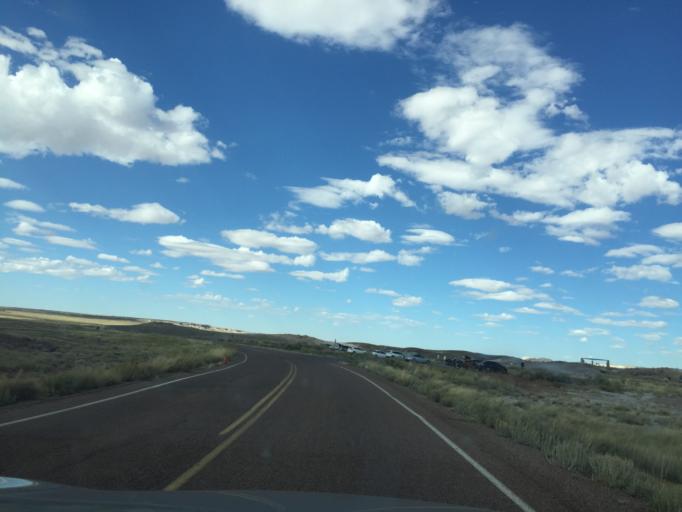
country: US
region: Arizona
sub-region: Navajo County
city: Holbrook
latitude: 34.8628
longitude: -109.7924
